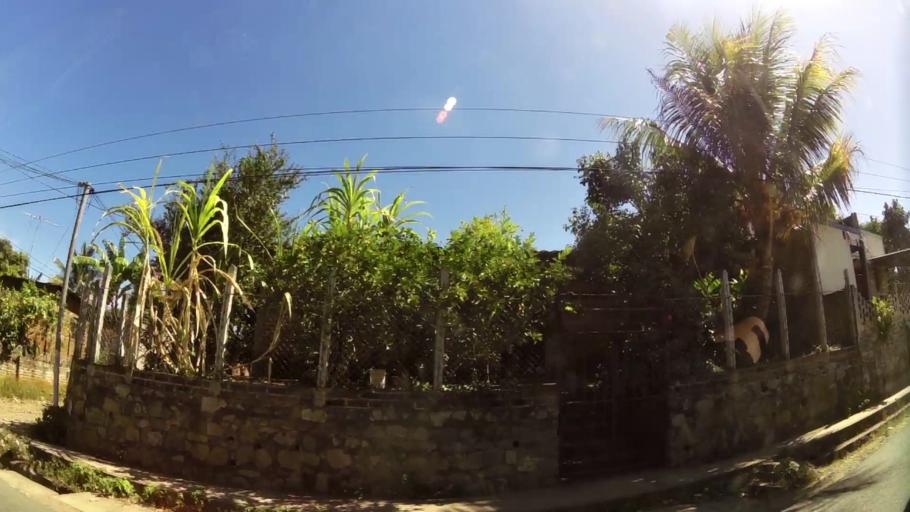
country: SV
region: Ahuachapan
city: Ahuachapan
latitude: 13.9274
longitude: -89.8425
